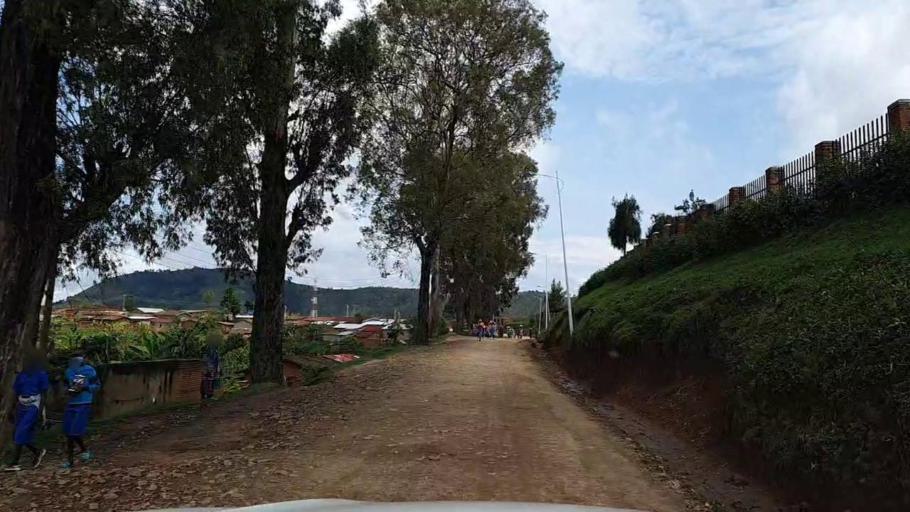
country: RW
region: Southern Province
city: Gikongoro
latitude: -2.3325
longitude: 29.5250
